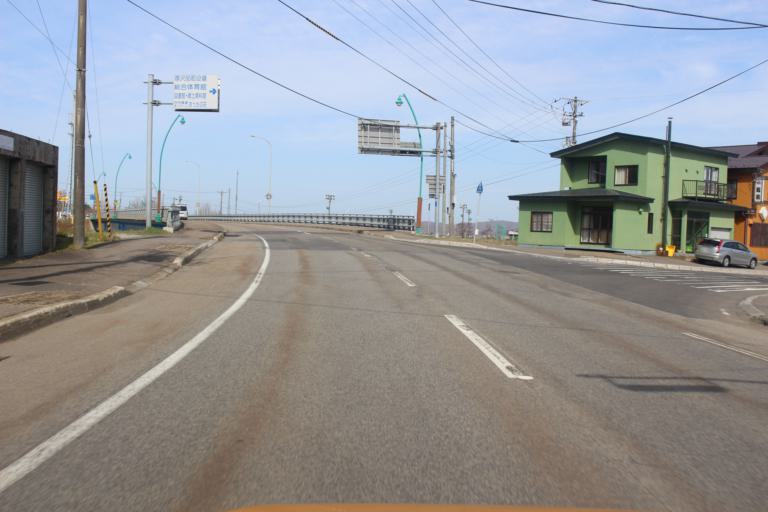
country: JP
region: Hokkaido
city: Kamiiso
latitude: 41.9170
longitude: 140.2233
